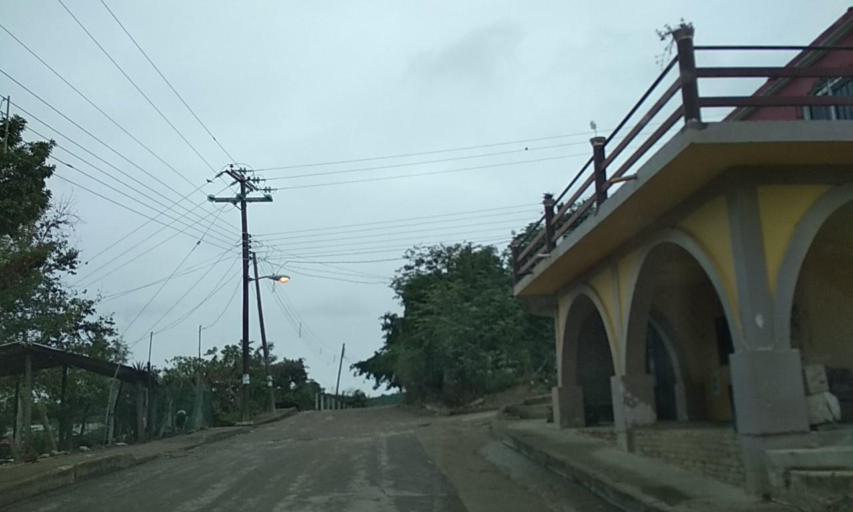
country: MX
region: Veracruz
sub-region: Papantla
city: El Chote
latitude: 20.3895
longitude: -97.3545
